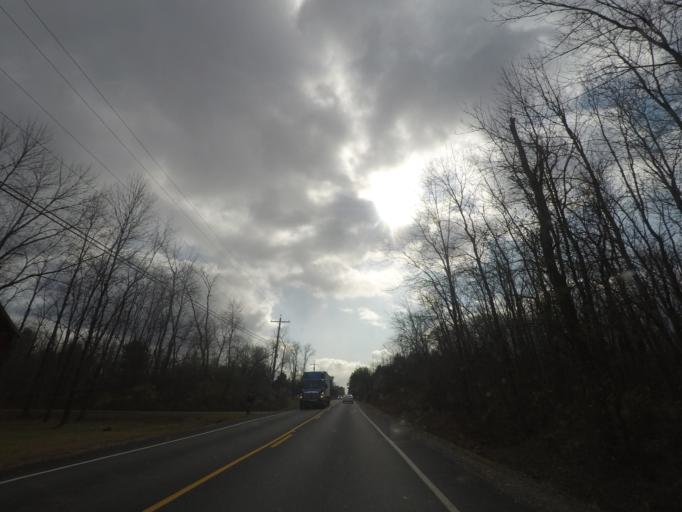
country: US
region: New York
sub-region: Saratoga County
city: Ballston Spa
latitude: 42.9695
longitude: -73.8307
